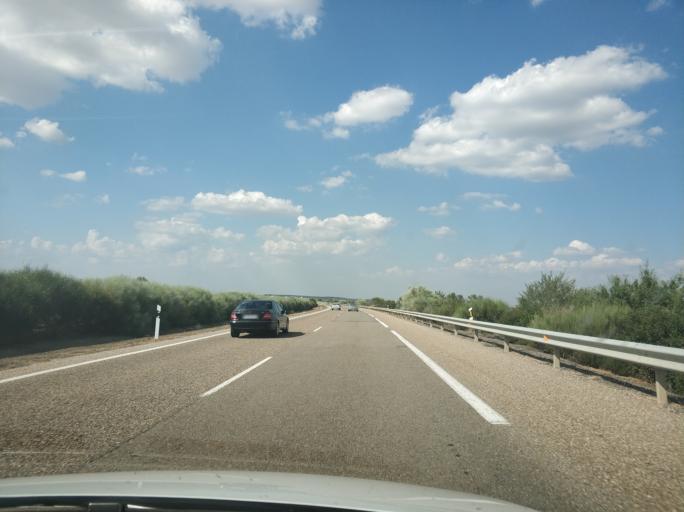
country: ES
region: Castille and Leon
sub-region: Provincia de Zamora
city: Matilla de Arzon
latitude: 42.0758
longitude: -5.6575
